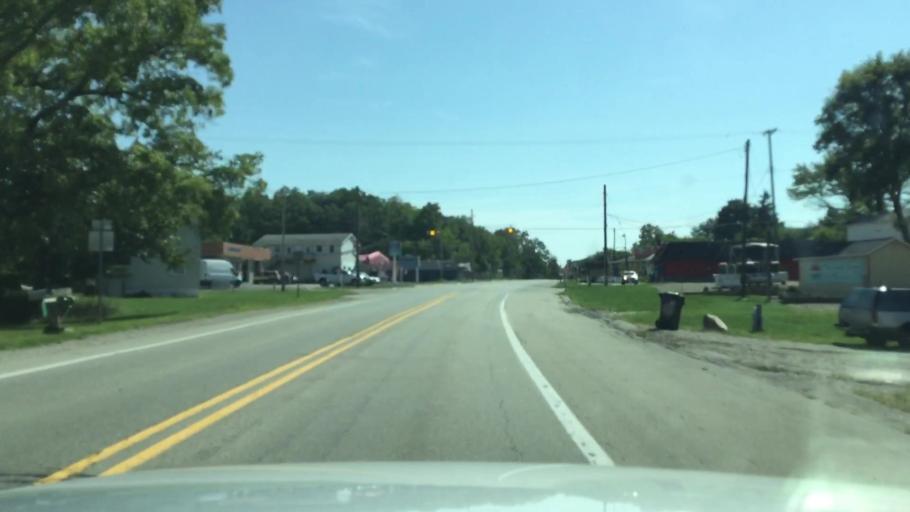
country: US
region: Michigan
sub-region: Lenawee County
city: Manitou Beach-Devils Lake
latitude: 42.0083
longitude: -84.2937
